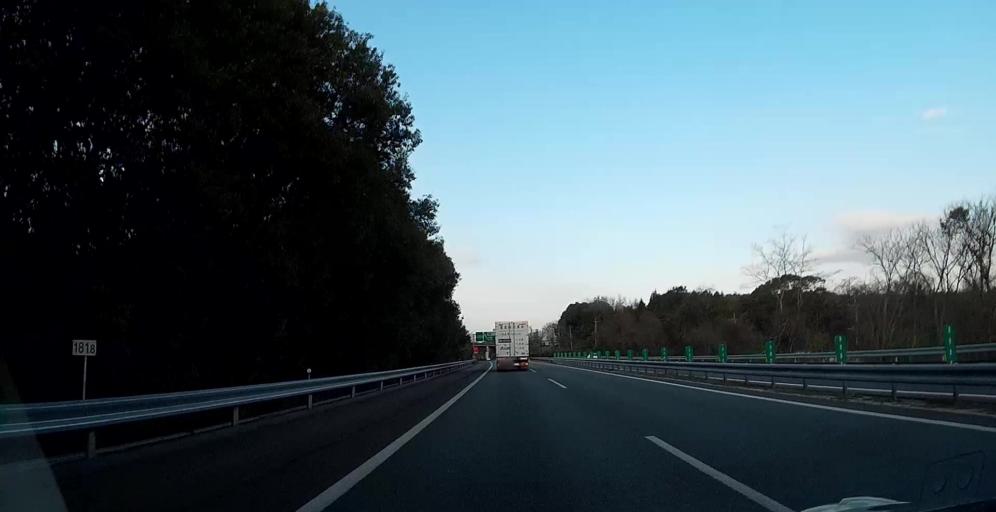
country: JP
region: Kumamoto
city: Kumamoto
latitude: 32.7444
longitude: 130.7855
